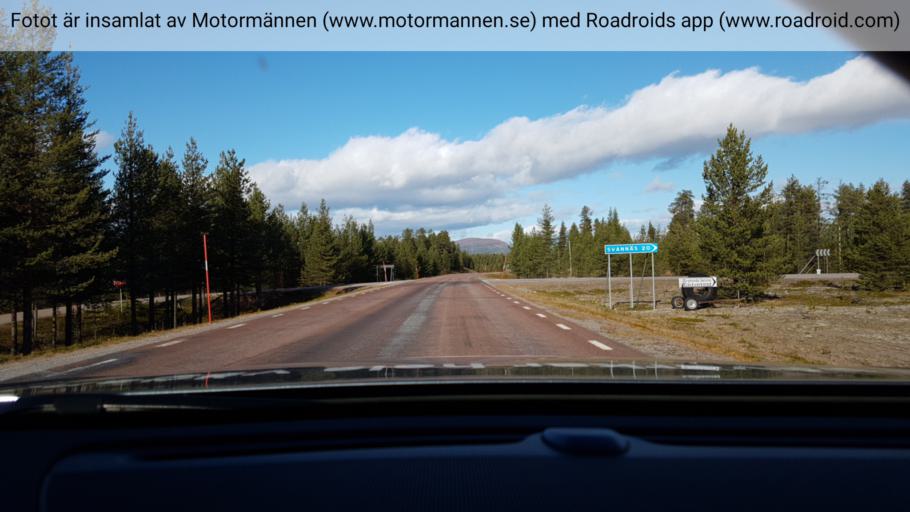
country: SE
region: Norrbotten
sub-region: Arjeplogs Kommun
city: Arjeplog
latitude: 66.0407
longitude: 18.0399
